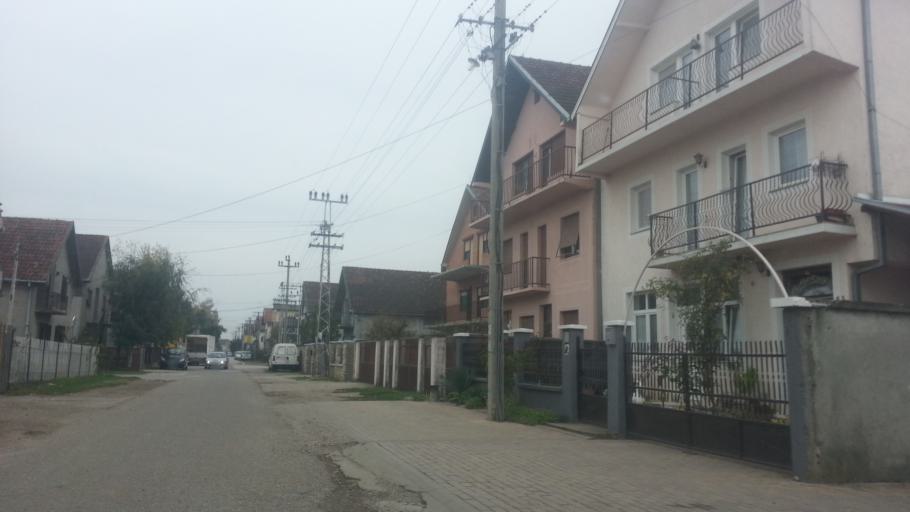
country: RS
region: Autonomna Pokrajina Vojvodina
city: Nova Pazova
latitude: 44.9539
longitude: 20.2122
